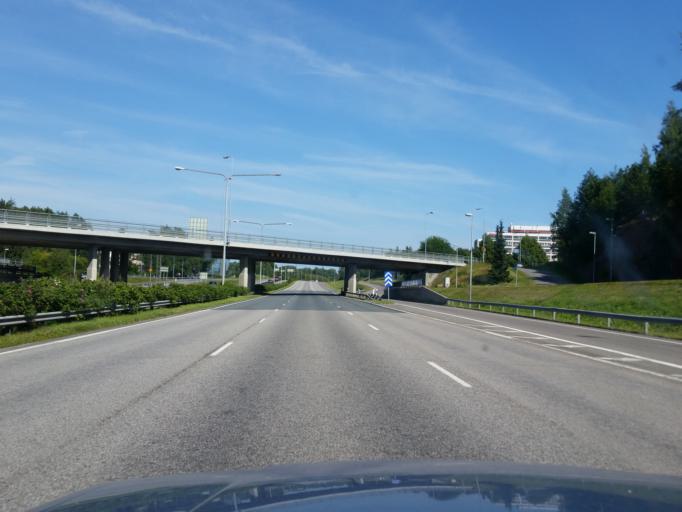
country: FI
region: Uusimaa
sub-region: Helsinki
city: Koukkuniemi
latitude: 60.1672
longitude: 24.7674
